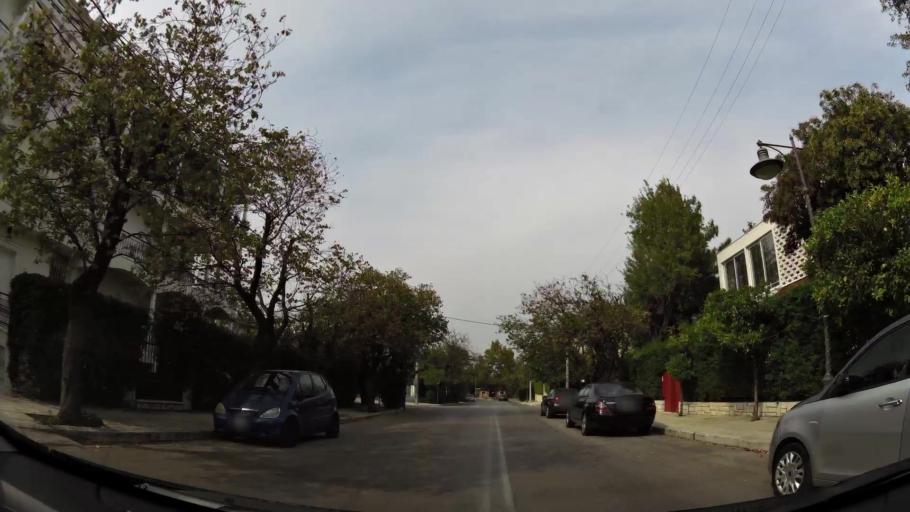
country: GR
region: Attica
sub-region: Nomarchia Athinas
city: Filothei
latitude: 38.0205
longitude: 23.7842
